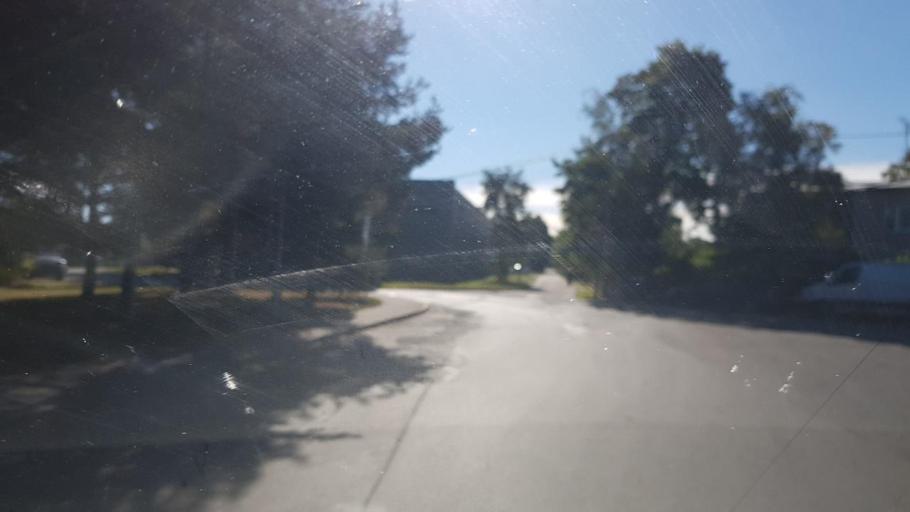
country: EE
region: Harju
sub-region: Tallinna linn
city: Tallinn
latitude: 59.4082
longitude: 24.8087
